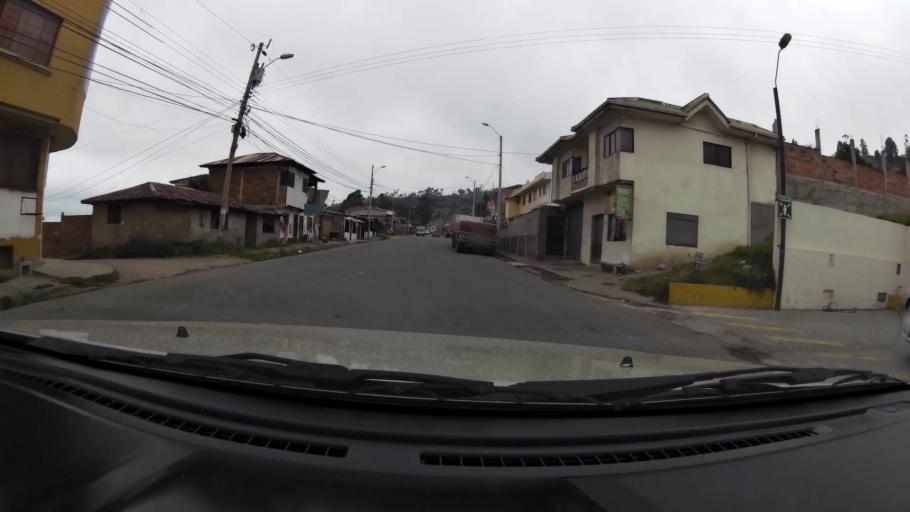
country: EC
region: Canar
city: Canar
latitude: -2.5033
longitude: -78.9274
